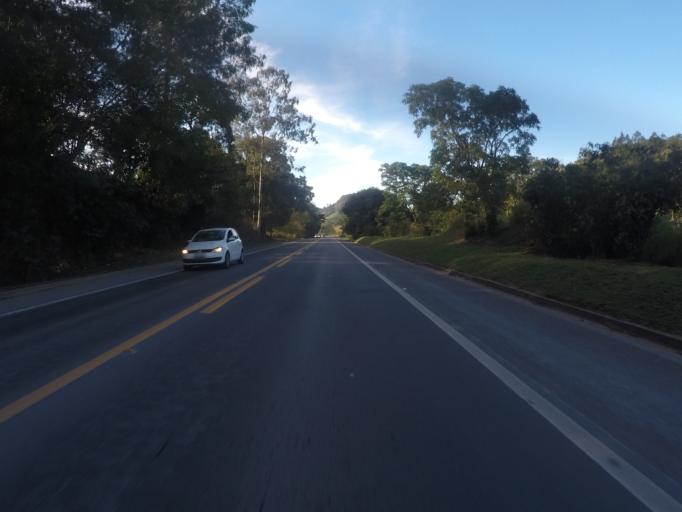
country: BR
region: Espirito Santo
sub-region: Fundao
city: Fundao
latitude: -19.8767
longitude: -40.4152
